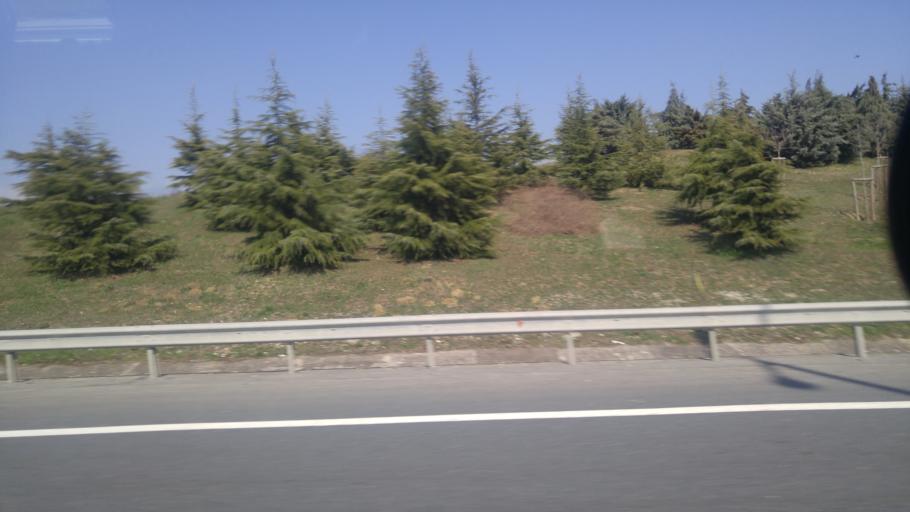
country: TR
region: Istanbul
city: Selimpasa
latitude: 41.0682
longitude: 28.3893
